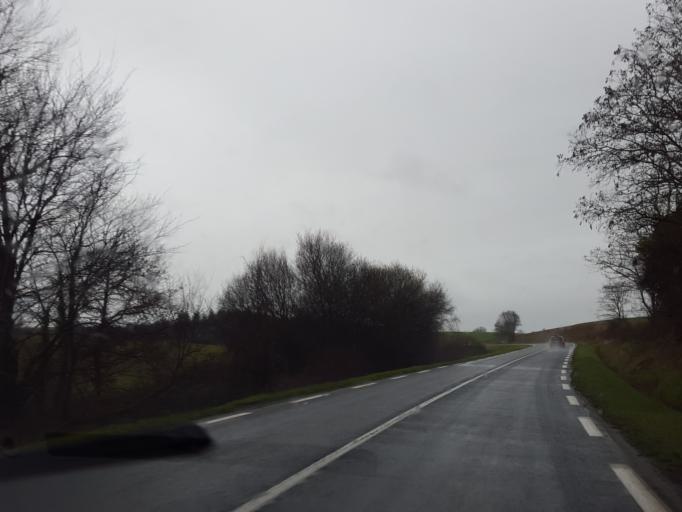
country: FR
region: Midi-Pyrenees
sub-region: Departement de l'Ariege
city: Mirepoix
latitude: 43.1536
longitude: 1.9769
